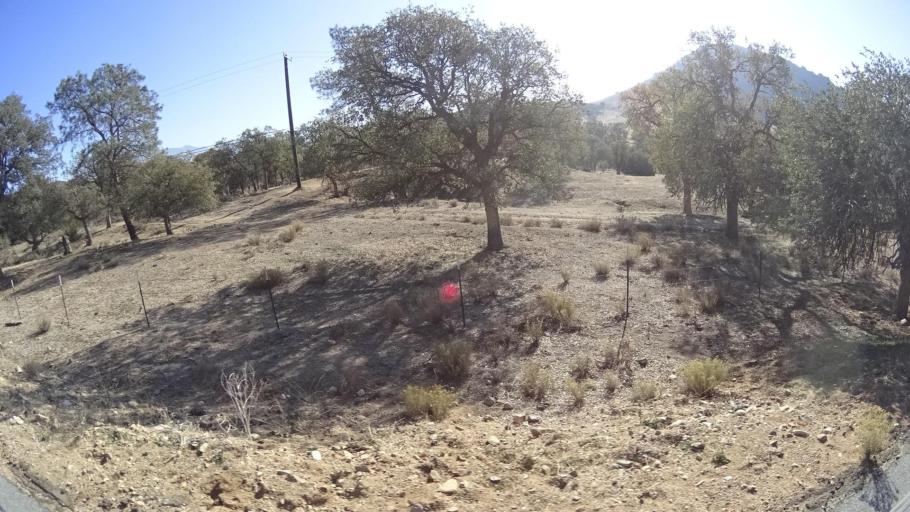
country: US
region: California
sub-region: Kern County
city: Tehachapi
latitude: 35.3393
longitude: -118.3876
